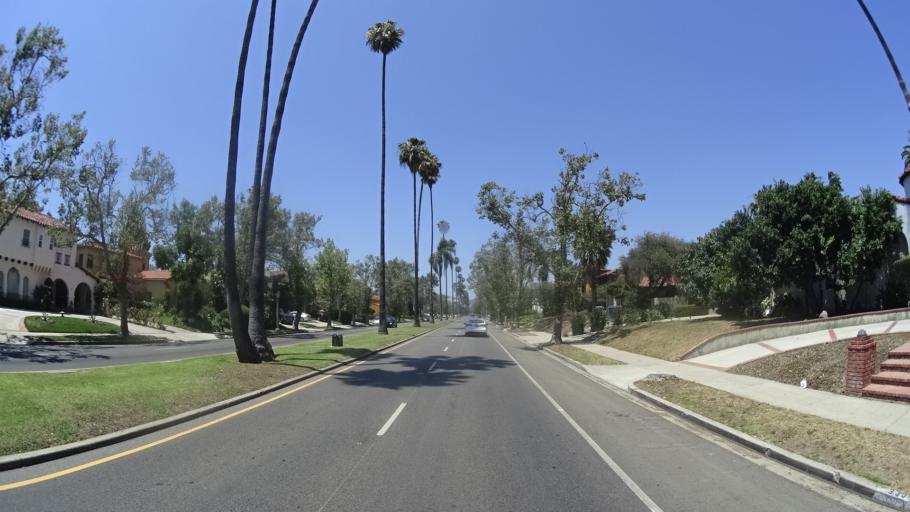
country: US
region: California
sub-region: Los Angeles County
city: Hollywood
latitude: 34.0771
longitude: -118.3385
